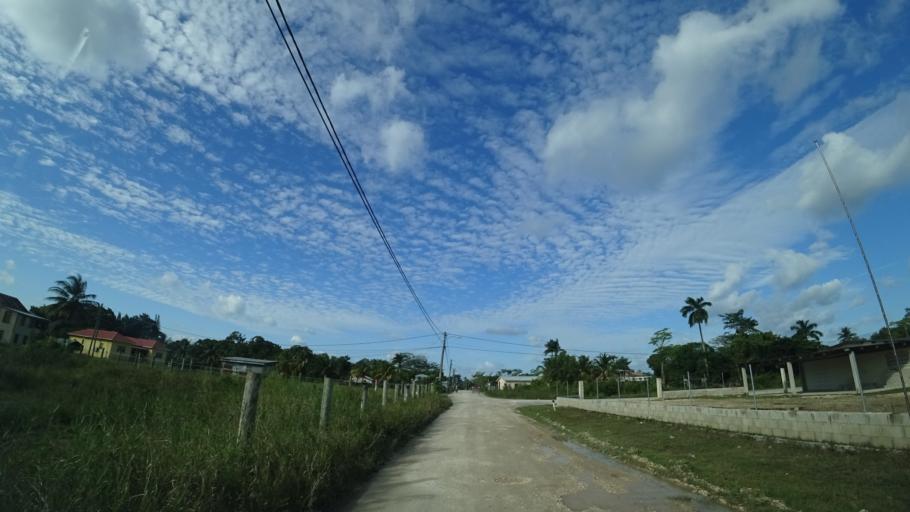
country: BZ
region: Belize
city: Belize City
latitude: 17.5671
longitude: -88.4086
